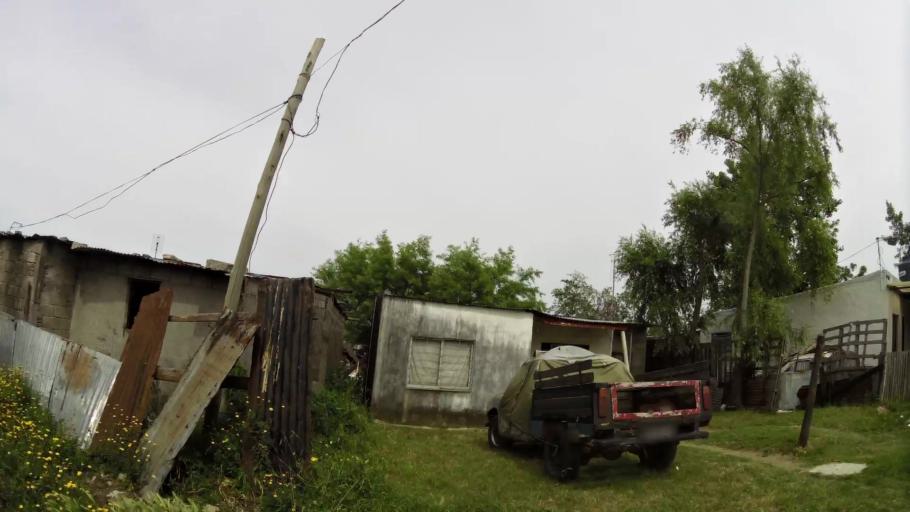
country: UY
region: Montevideo
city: Montevideo
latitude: -34.8362
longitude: -56.1781
